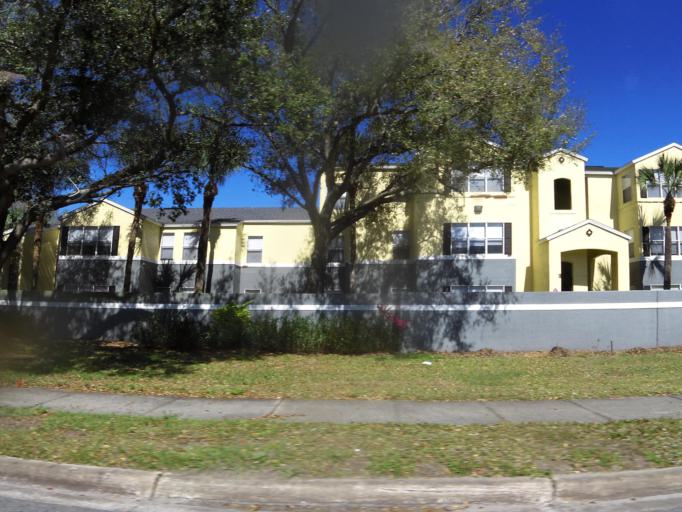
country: US
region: Florida
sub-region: Seminole County
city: Sanford
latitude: 28.8117
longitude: -81.2885
